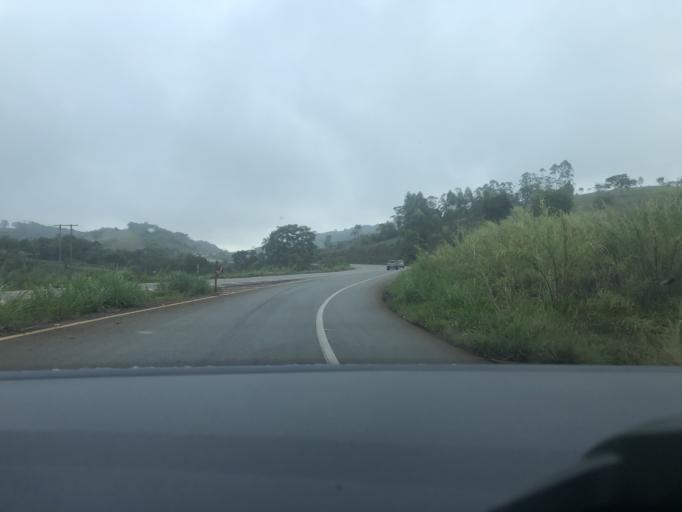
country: BR
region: Minas Gerais
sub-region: Congonhas
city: Congonhas
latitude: -20.6007
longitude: -43.9358
